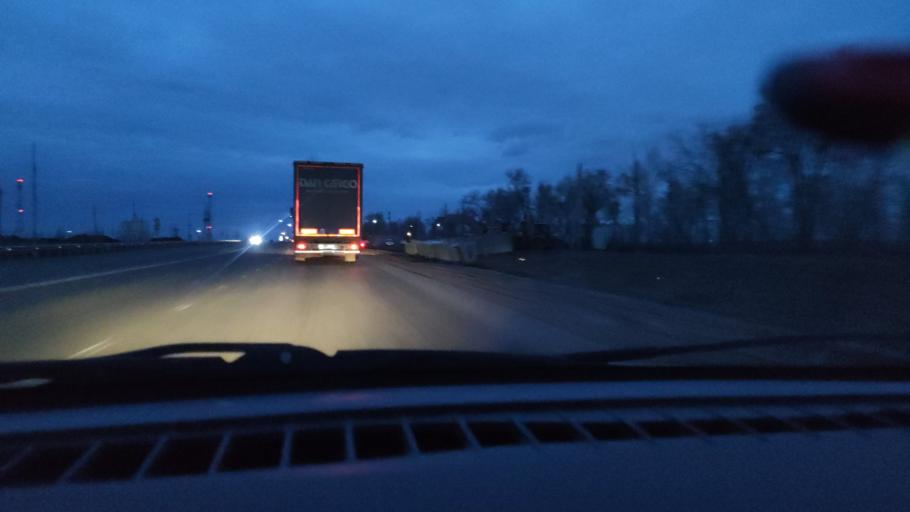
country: RU
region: Orenburg
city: Tatarskaya Kargala
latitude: 51.9718
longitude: 55.1860
